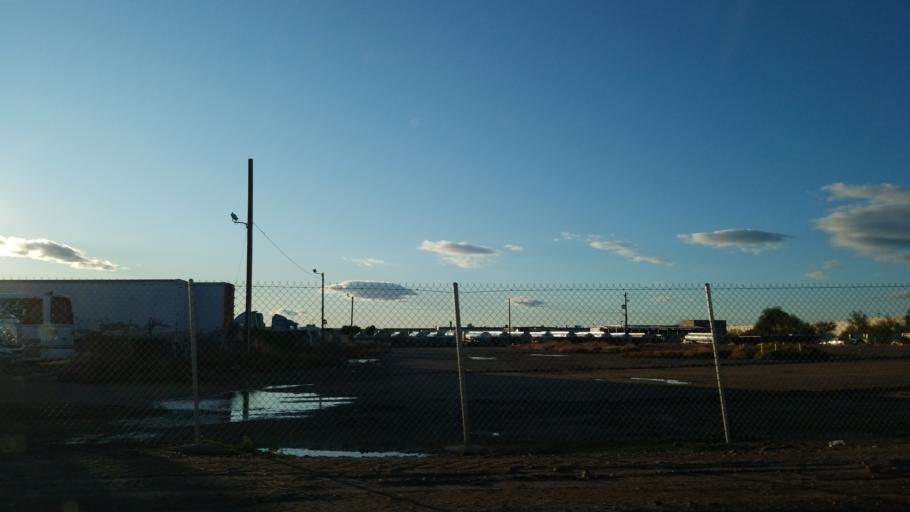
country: US
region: Arizona
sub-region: Maricopa County
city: Tolleson
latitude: 33.4394
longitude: -112.1879
